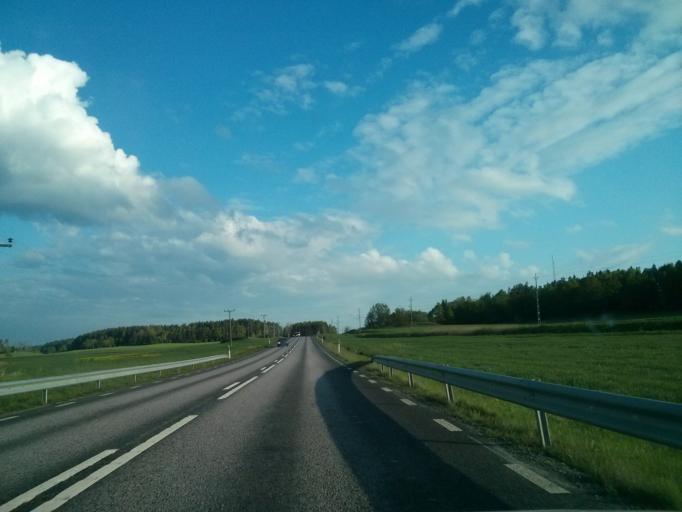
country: SE
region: Soedermanland
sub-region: Nykopings Kommun
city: Olstorp
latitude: 58.8780
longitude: 16.6713
